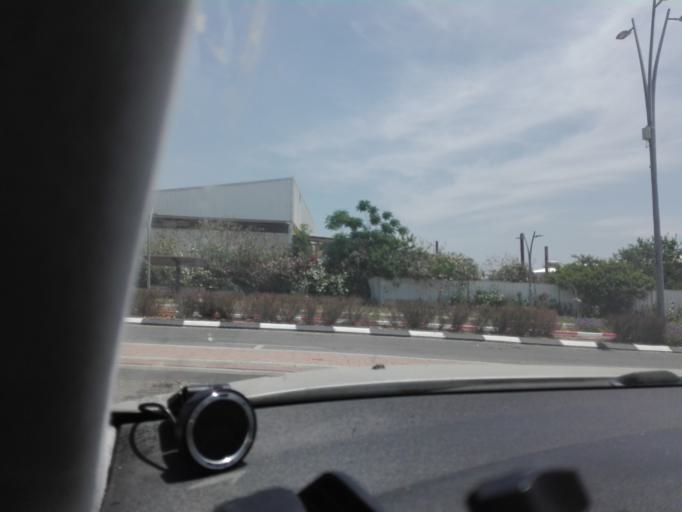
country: IL
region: Central District
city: Bene 'Ayish
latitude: 31.7372
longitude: 34.7495
